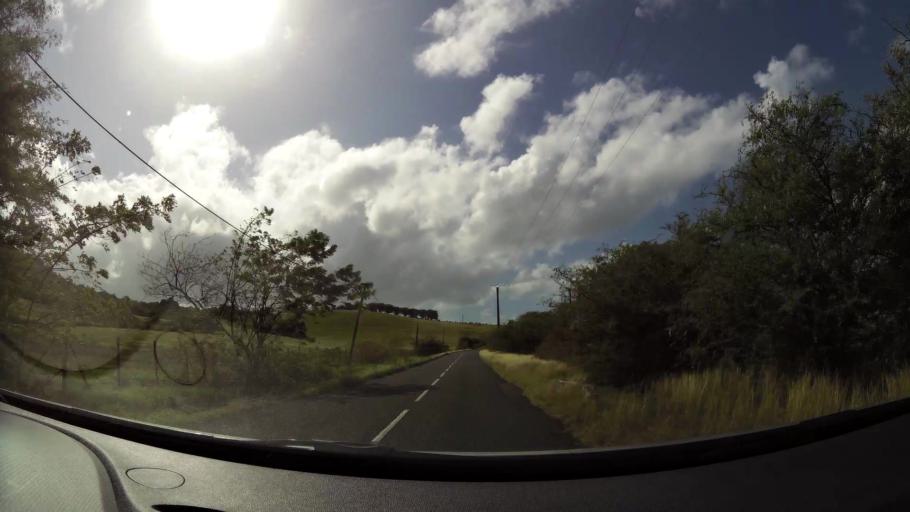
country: MQ
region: Martinique
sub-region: Martinique
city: Le Marin
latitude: 14.4158
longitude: -60.8780
